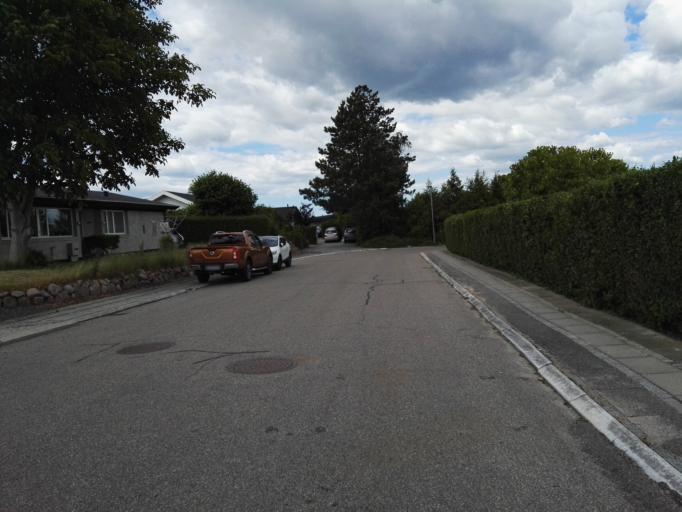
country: DK
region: Capital Region
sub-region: Egedal Kommune
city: Stenlose
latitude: 55.7725
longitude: 12.1866
